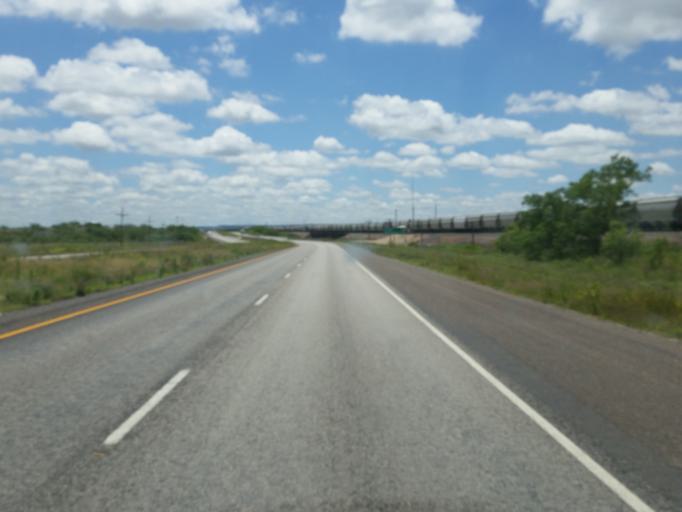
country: US
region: Texas
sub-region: Garza County
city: Post
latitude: 33.0416
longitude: -101.2019
